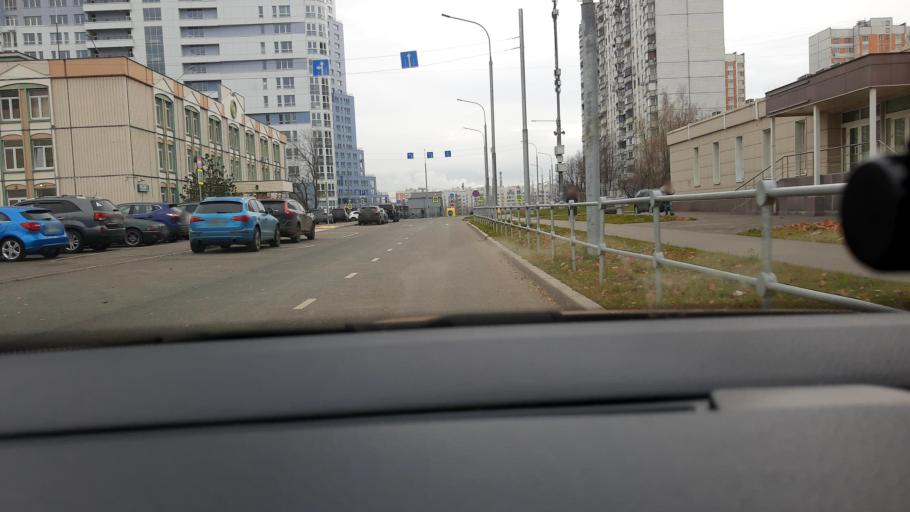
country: RU
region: Moskovskaya
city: Khoroshevo-Mnevniki
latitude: 55.7712
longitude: 37.4943
